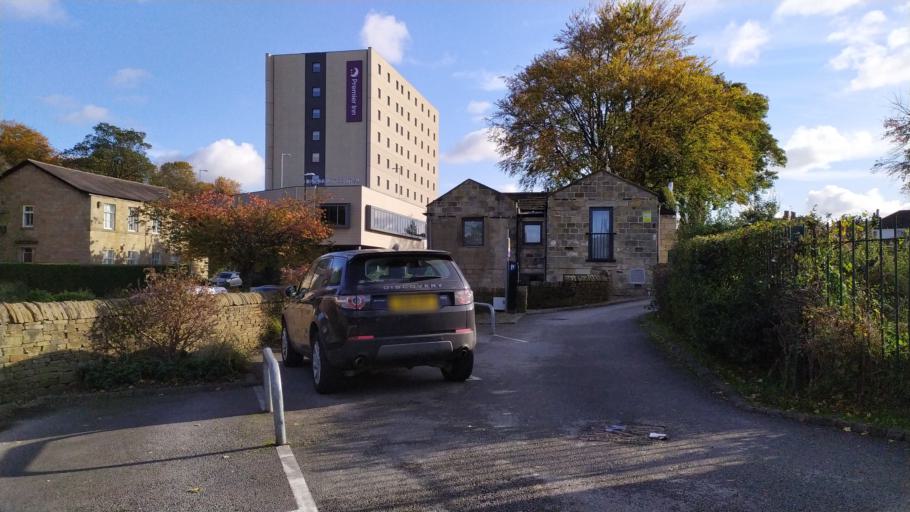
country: GB
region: England
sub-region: City and Borough of Leeds
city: Leeds
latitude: 53.8233
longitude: -1.5800
